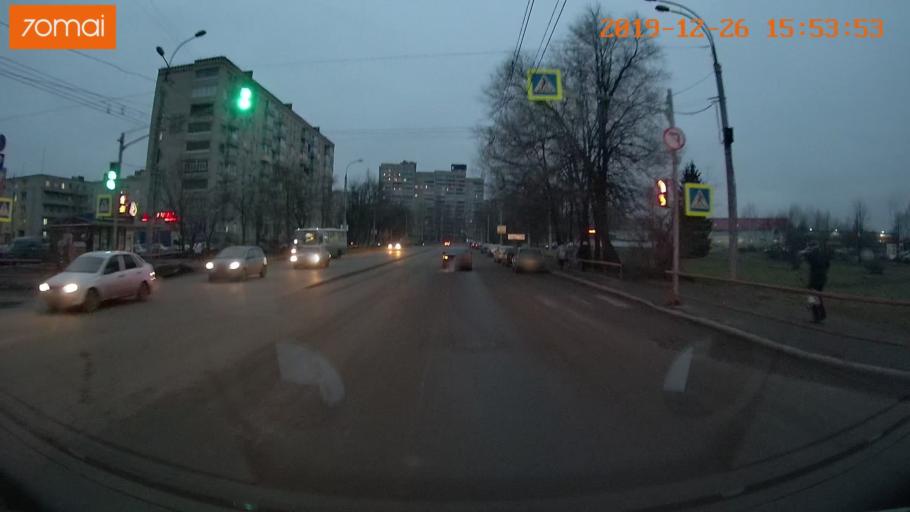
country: RU
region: Jaroslavl
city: Rybinsk
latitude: 58.0479
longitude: 38.8225
